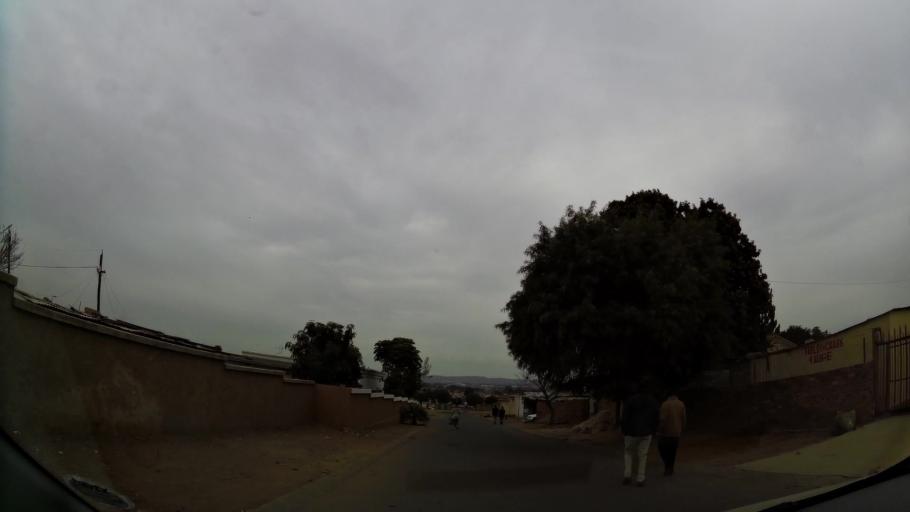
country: ZA
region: Gauteng
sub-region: City of Tshwane Metropolitan Municipality
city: Pretoria
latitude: -25.7019
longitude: 28.3341
